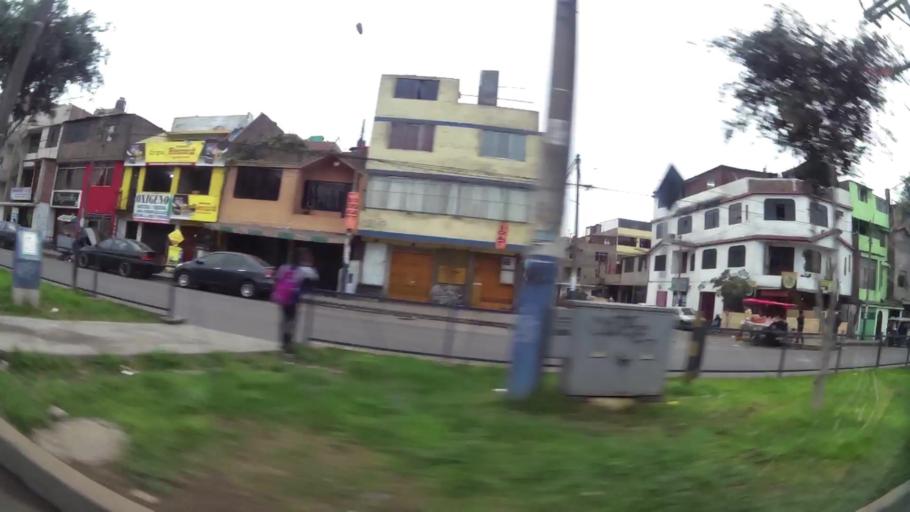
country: PE
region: Lima
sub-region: Lima
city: San Luis
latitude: -12.0691
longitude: -76.9804
